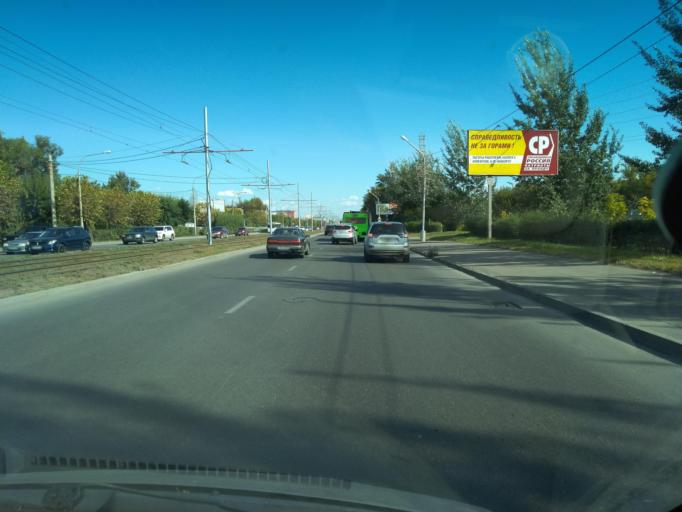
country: RU
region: Krasnoyarskiy
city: Solnechnyy
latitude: 56.0178
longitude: 92.9931
